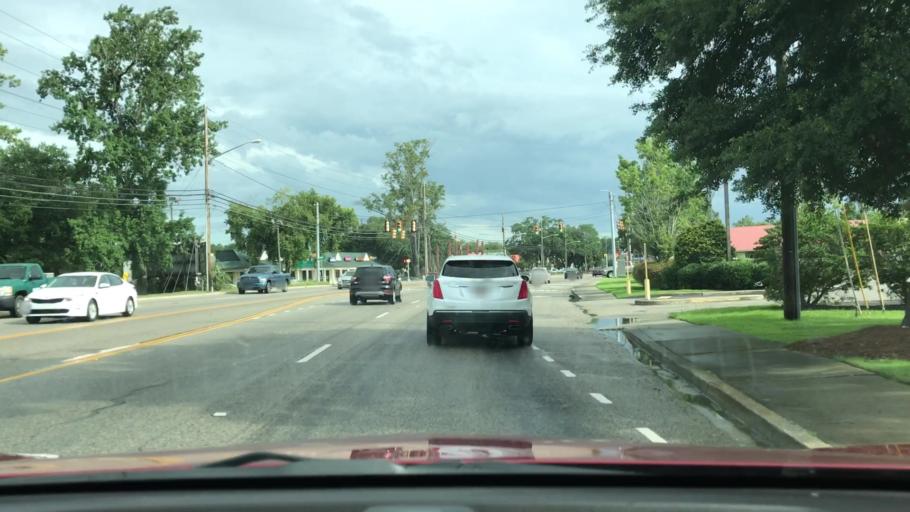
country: US
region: South Carolina
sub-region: Georgetown County
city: Georgetown
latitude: 33.3868
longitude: -79.2887
